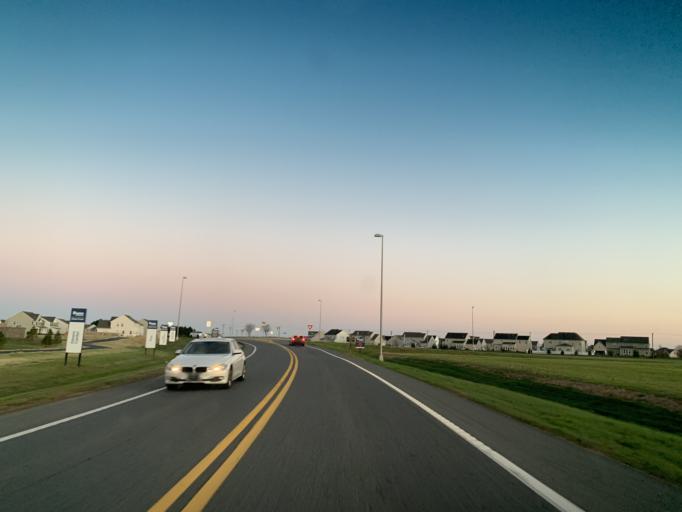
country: US
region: Delaware
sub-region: New Castle County
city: Middletown
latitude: 39.4289
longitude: -75.7402
